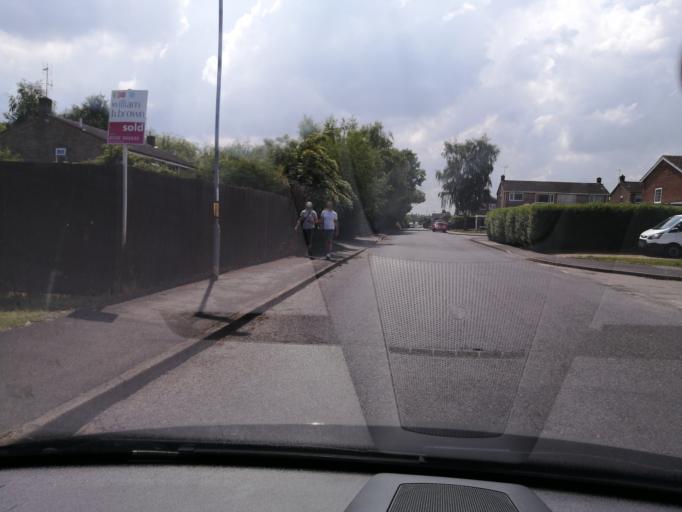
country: GB
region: England
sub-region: Cambridgeshire
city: Yaxley
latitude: 52.5168
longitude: -0.2449
